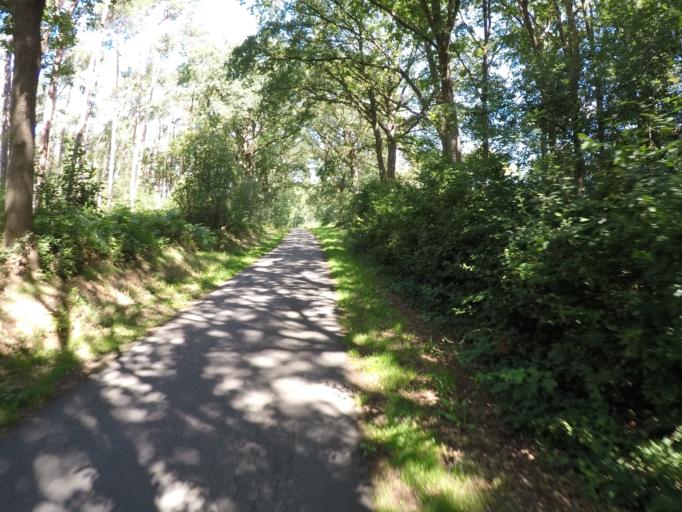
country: BE
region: Flanders
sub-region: Provincie Antwerpen
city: Herenthout
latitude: 51.1257
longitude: 4.7296
